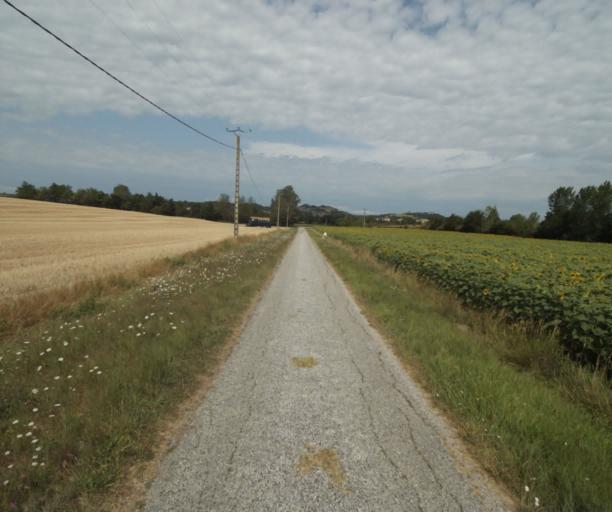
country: FR
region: Midi-Pyrenees
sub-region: Departement de la Haute-Garonne
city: Saint-Felix-Lauragais
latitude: 43.4209
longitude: 1.9120
